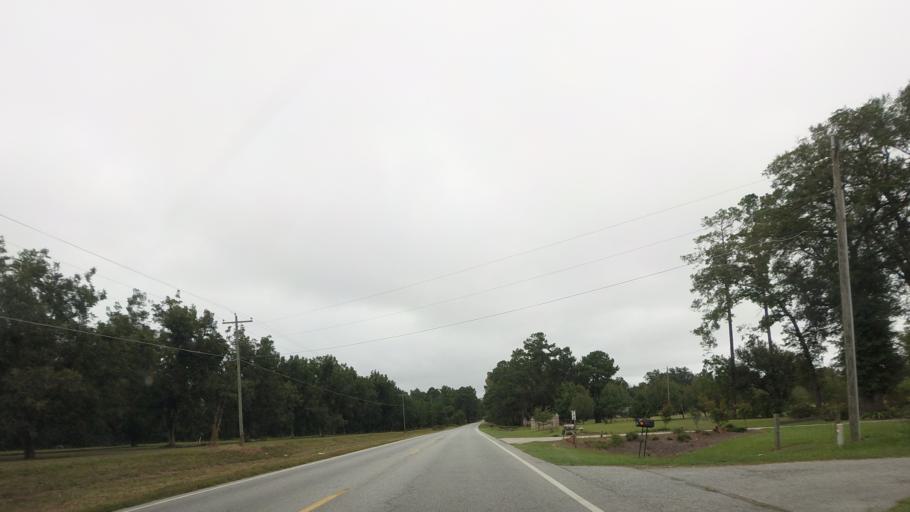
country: US
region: Georgia
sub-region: Berrien County
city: Ray City
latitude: 31.0470
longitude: -83.1979
